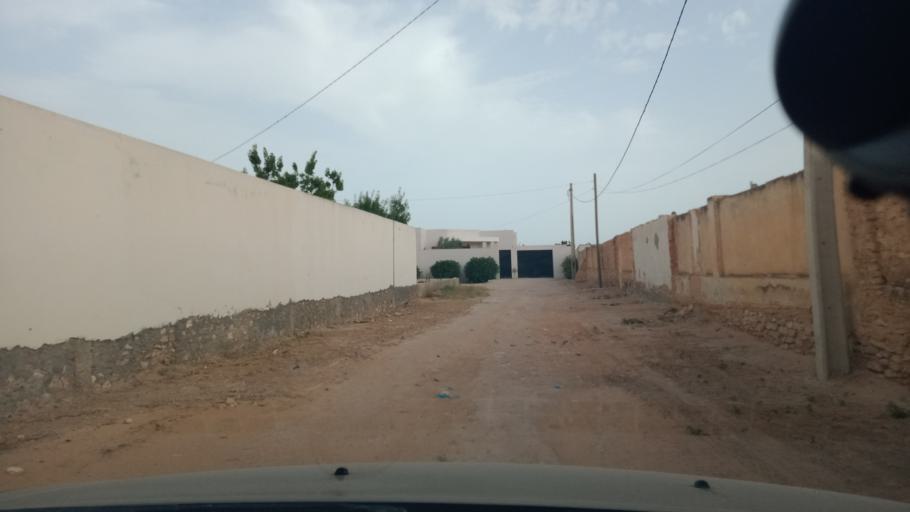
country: TN
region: Safaqis
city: Al Qarmadah
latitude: 34.7856
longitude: 10.7642
